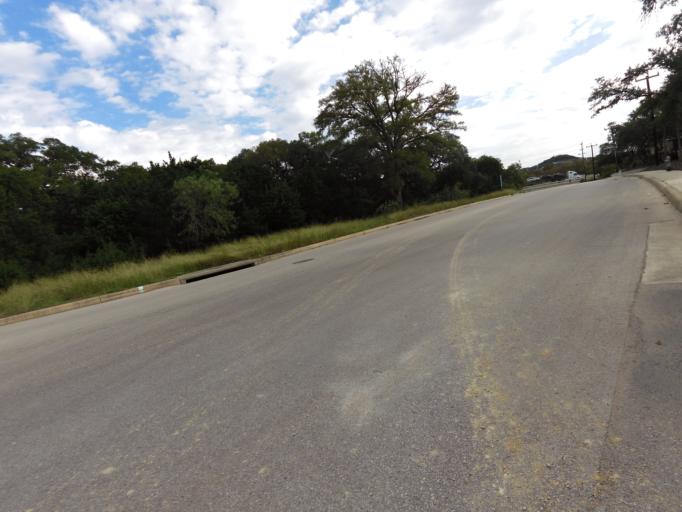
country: US
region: Texas
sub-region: Bexar County
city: Cross Mountain
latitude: 29.6455
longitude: -98.6228
